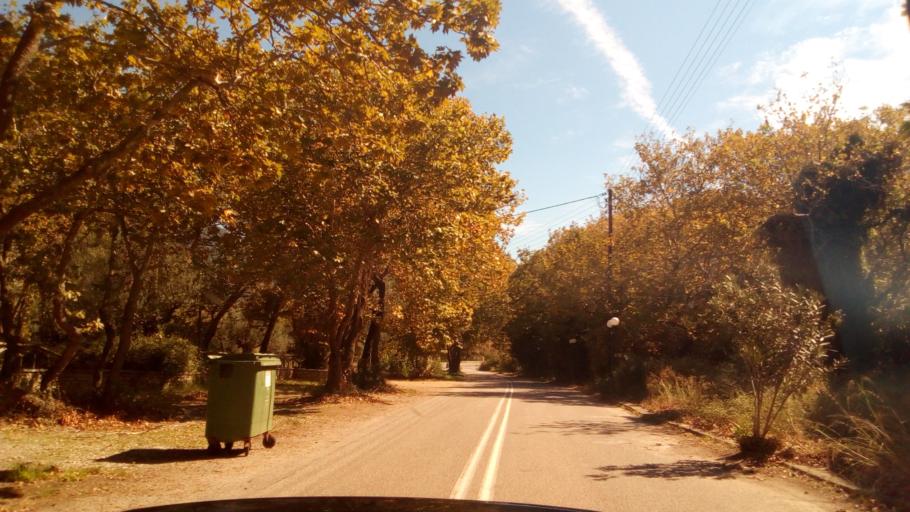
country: GR
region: West Greece
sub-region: Nomos Achaias
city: Kamarai
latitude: 38.3899
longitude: 22.0599
